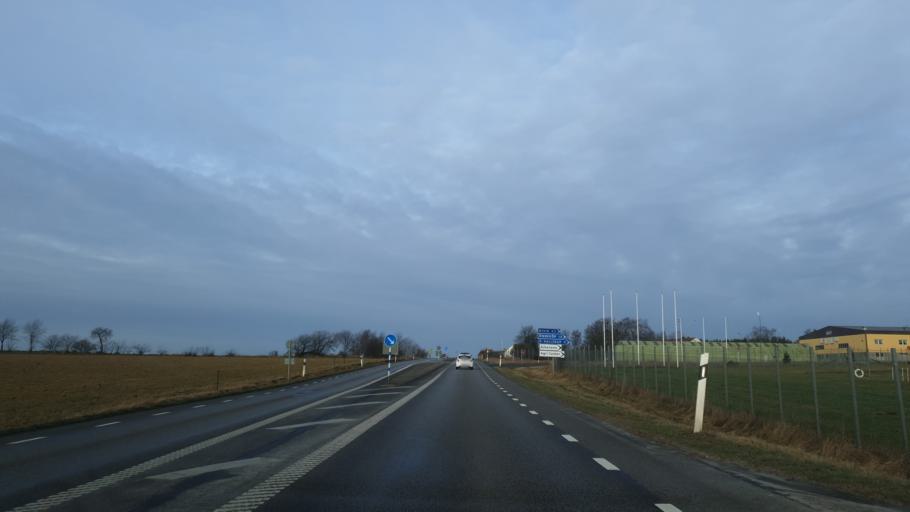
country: SE
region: Skane
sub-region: Horby Kommun
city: Hoerby
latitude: 55.7898
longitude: 13.6763
